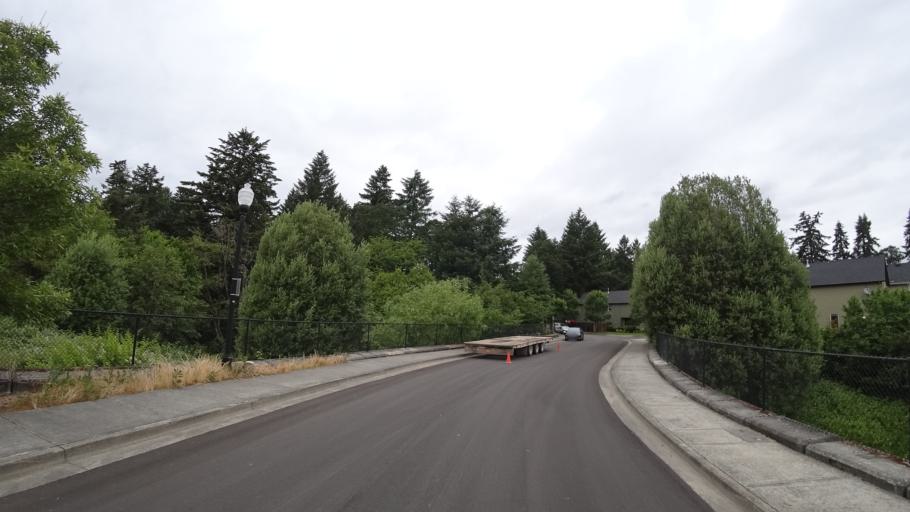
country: US
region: Oregon
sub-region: Washington County
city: Hillsboro
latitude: 45.4962
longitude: -122.9370
